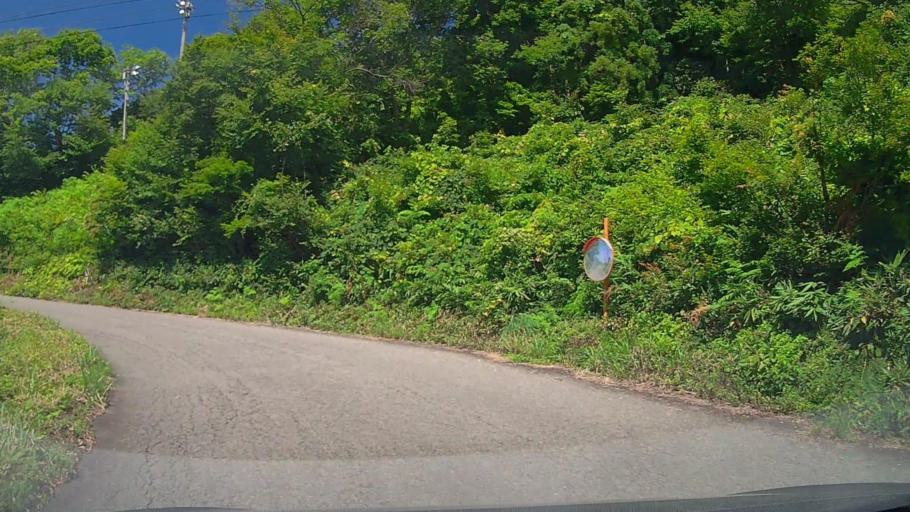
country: JP
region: Nagano
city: Iiyama
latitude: 36.9333
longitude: 138.4565
